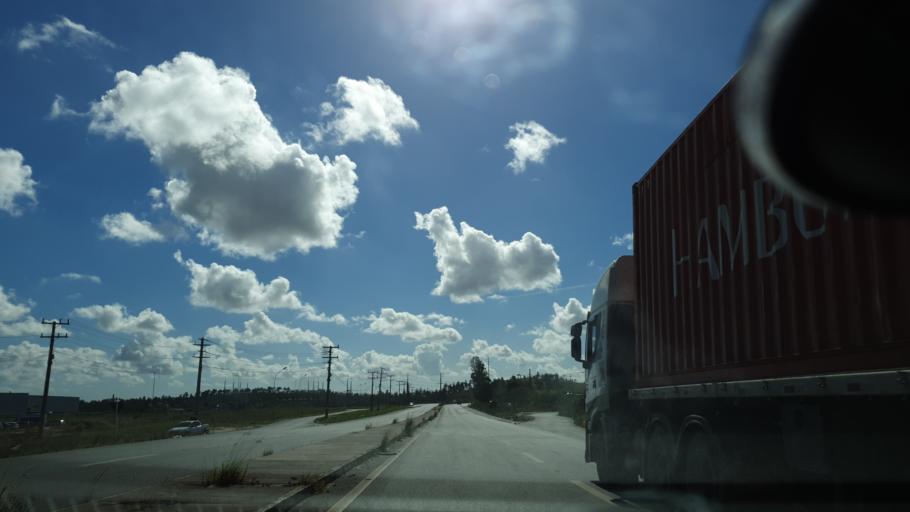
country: BR
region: Bahia
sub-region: Camacari
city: Camacari
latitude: -12.6838
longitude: -38.2676
